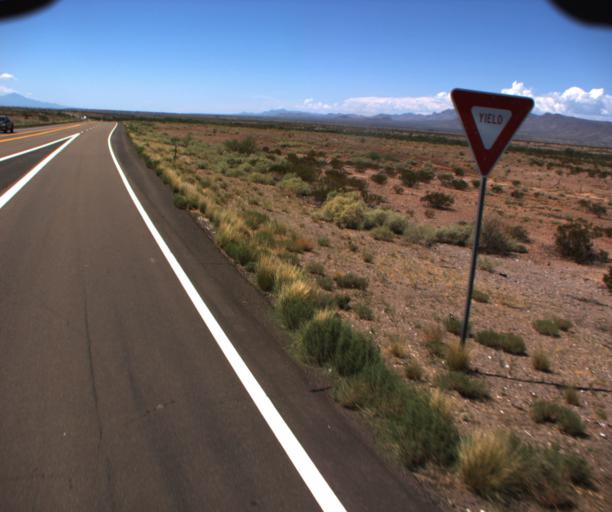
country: US
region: Arizona
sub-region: Graham County
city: Safford
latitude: 32.7933
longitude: -109.5528
